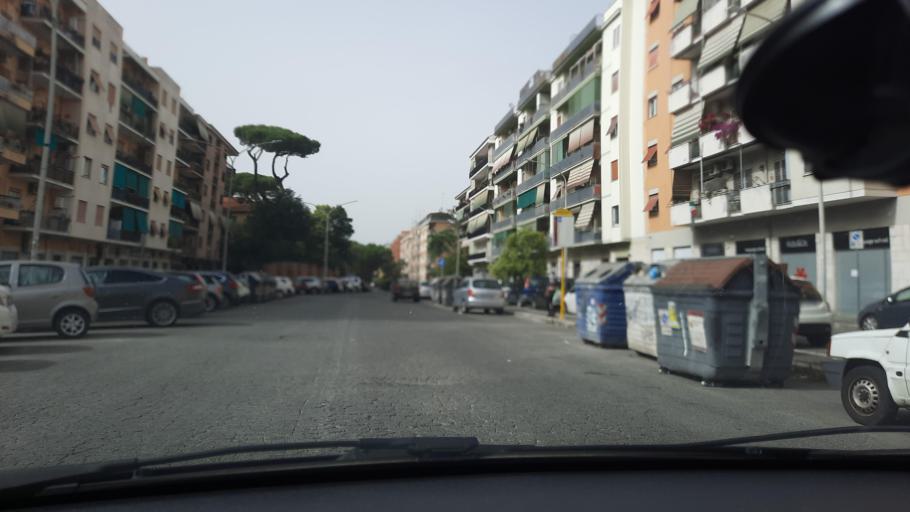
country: IT
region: Latium
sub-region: Citta metropolitana di Roma Capitale
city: Rome
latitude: 41.8528
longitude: 12.4802
